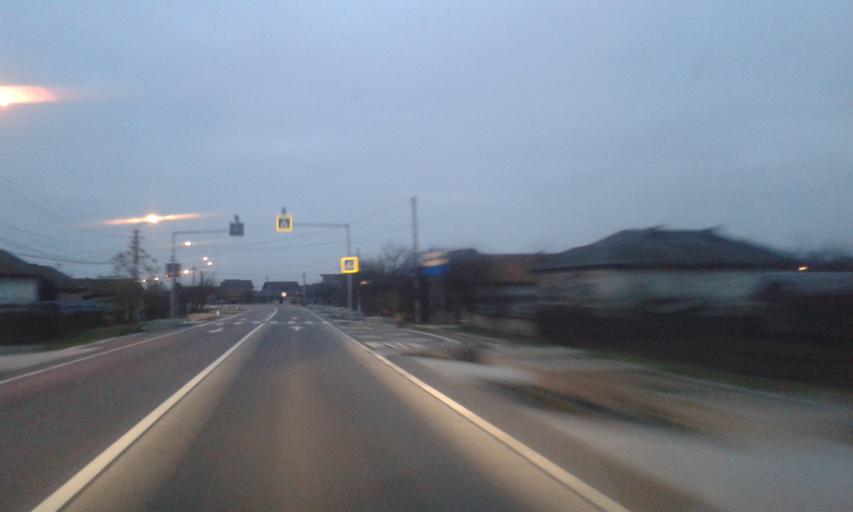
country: RO
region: Gorj
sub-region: Comuna Turcinesti
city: Turcinesti
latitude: 45.0862
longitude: 23.3198
